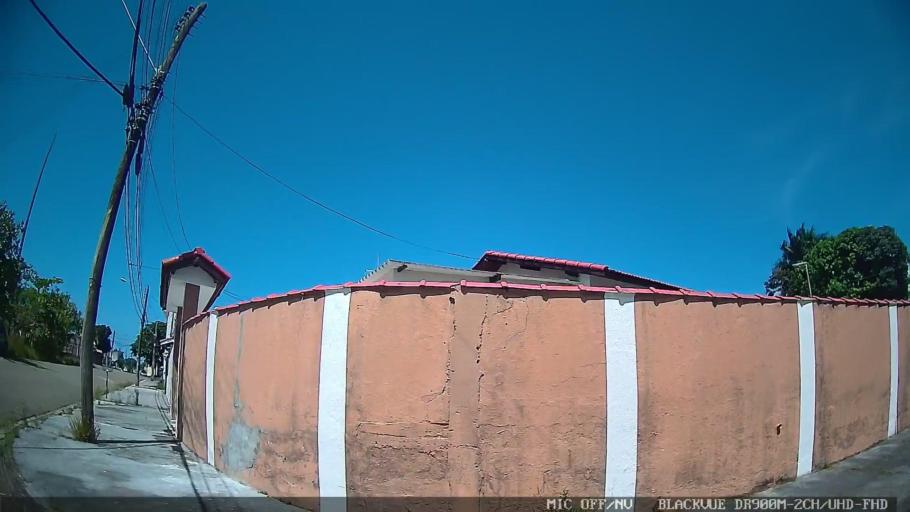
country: BR
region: Sao Paulo
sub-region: Peruibe
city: Peruibe
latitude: -24.3053
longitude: -46.9961
